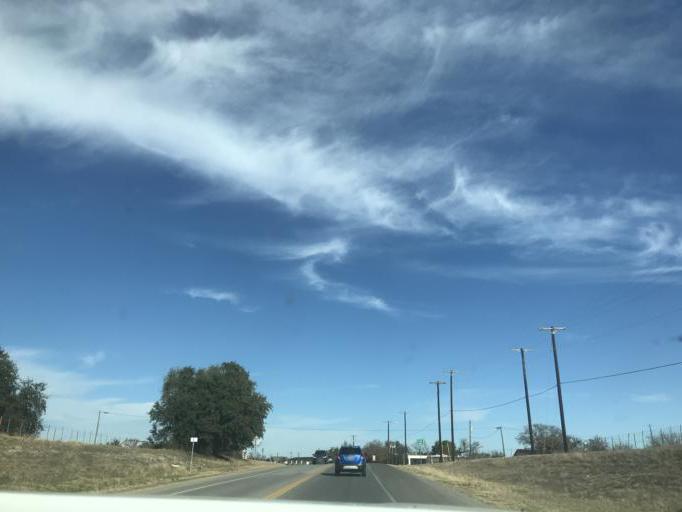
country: US
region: Texas
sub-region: Erath County
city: Stephenville
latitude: 32.2356
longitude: -98.2027
